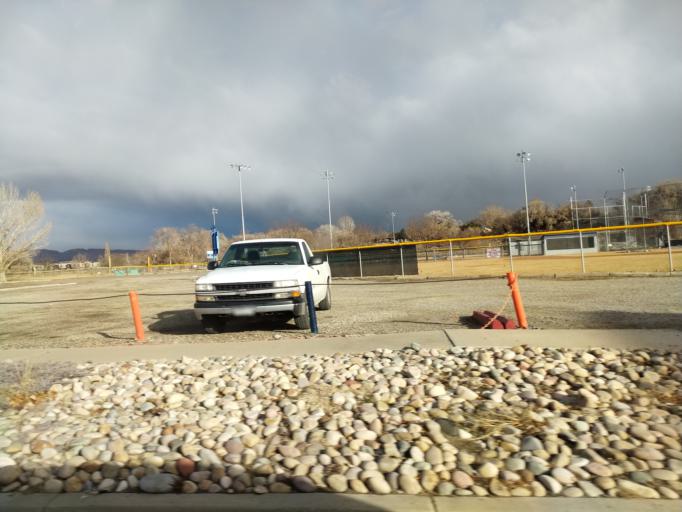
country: US
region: Colorado
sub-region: Mesa County
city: Grand Junction
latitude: 39.0875
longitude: -108.5801
